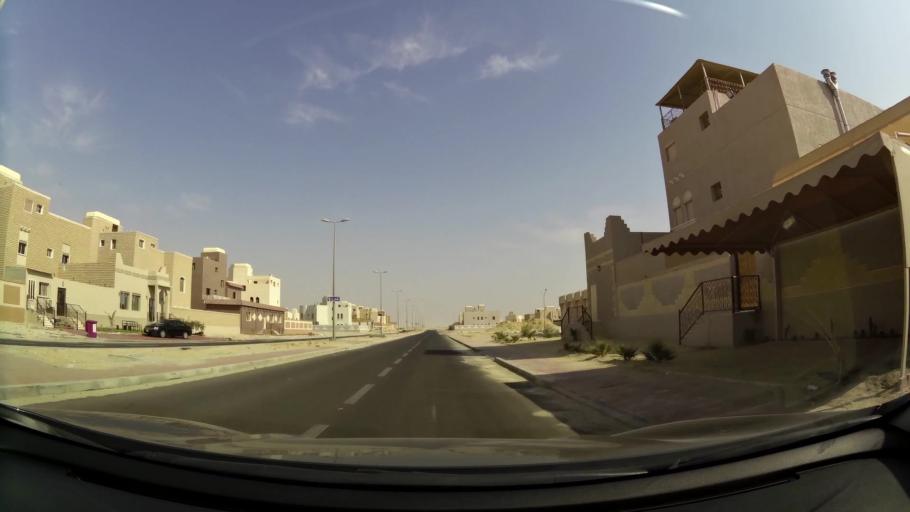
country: KW
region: Al Ahmadi
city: Al Wafrah
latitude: 28.7995
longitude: 48.0739
